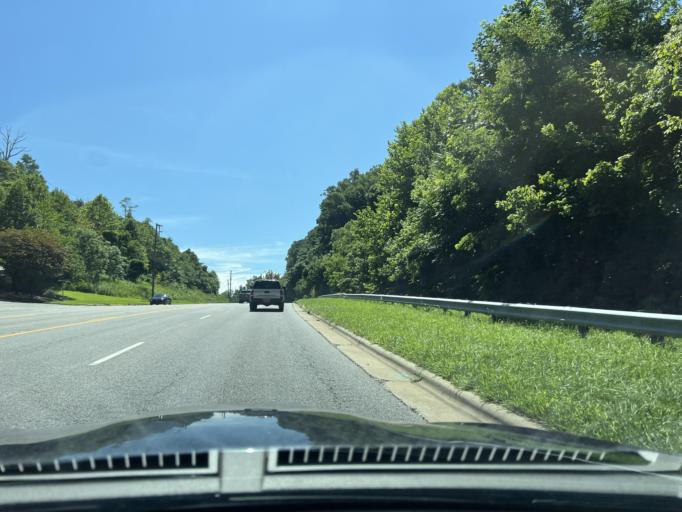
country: US
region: North Carolina
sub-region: Buncombe County
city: Fairview
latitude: 35.5471
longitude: -82.4562
